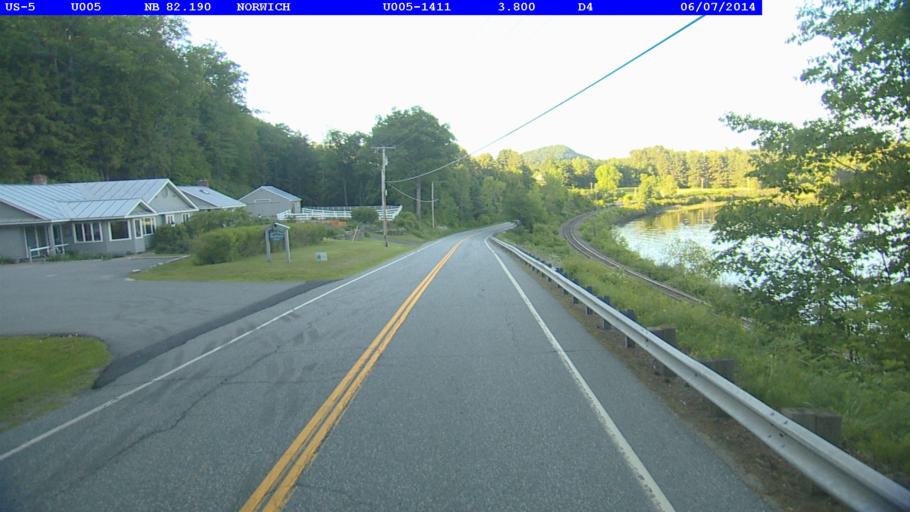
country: US
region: New Hampshire
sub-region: Grafton County
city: Hanover
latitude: 43.7328
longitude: -72.2731
